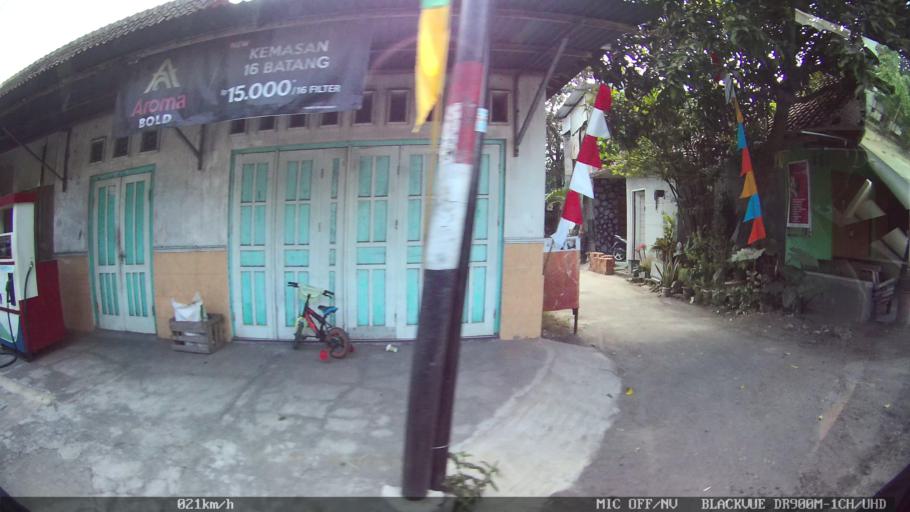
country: ID
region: Daerah Istimewa Yogyakarta
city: Bantul
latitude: -7.9080
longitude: 110.3454
